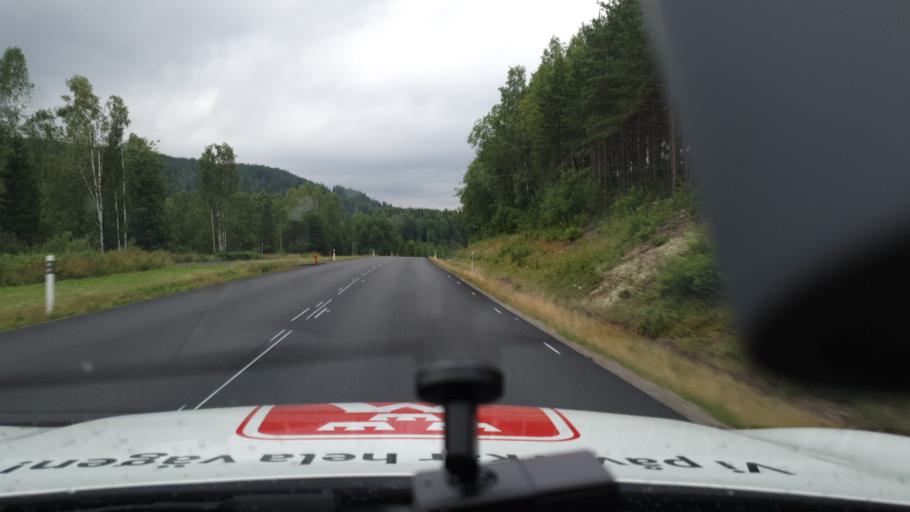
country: SE
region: Vaermland
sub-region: Torsby Kommun
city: Torsby
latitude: 60.2413
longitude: 13.0092
